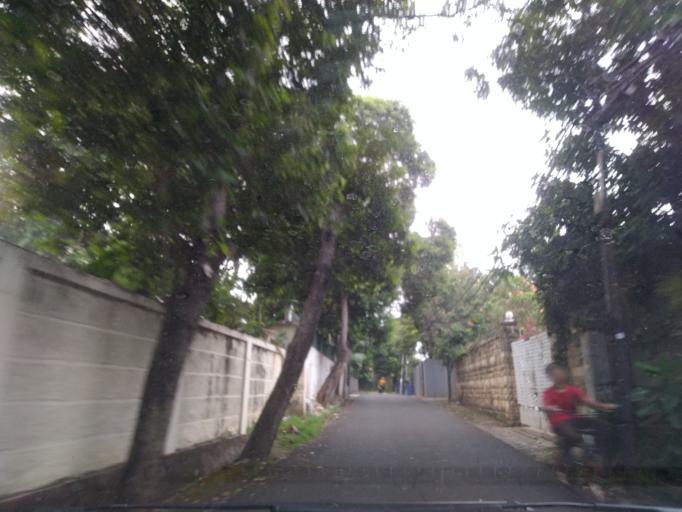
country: ID
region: Jakarta Raya
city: Jakarta
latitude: -6.2596
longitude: 106.8202
